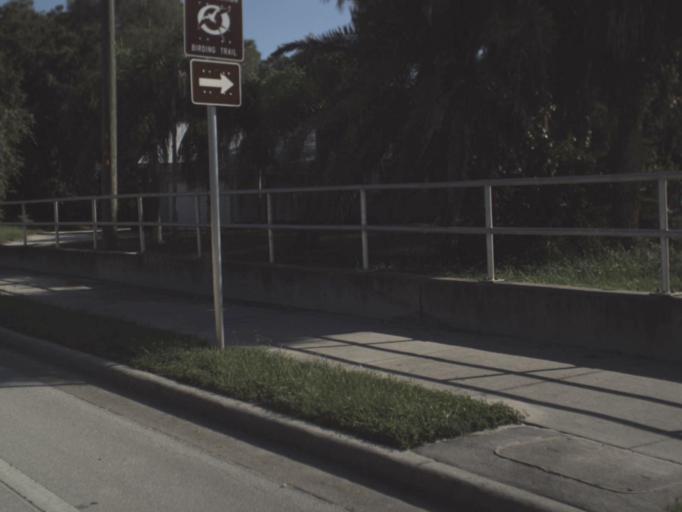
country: US
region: Florida
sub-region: Sarasota County
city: South Venice
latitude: 27.0229
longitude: -82.3930
